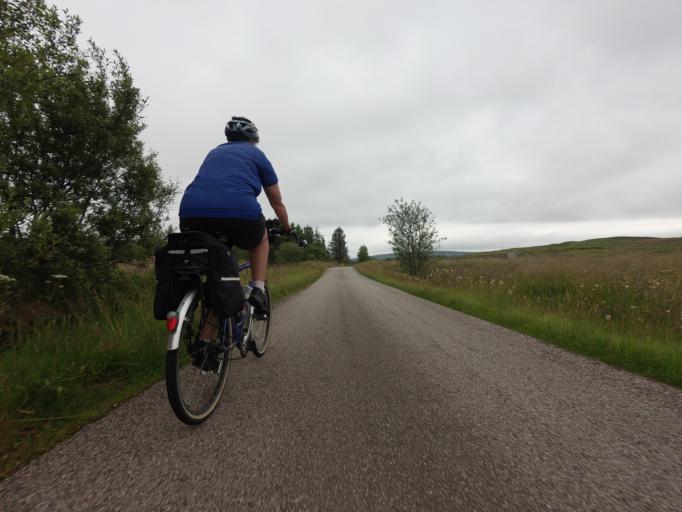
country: GB
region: Scotland
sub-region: Highland
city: Alness
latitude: 58.0102
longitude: -4.4030
